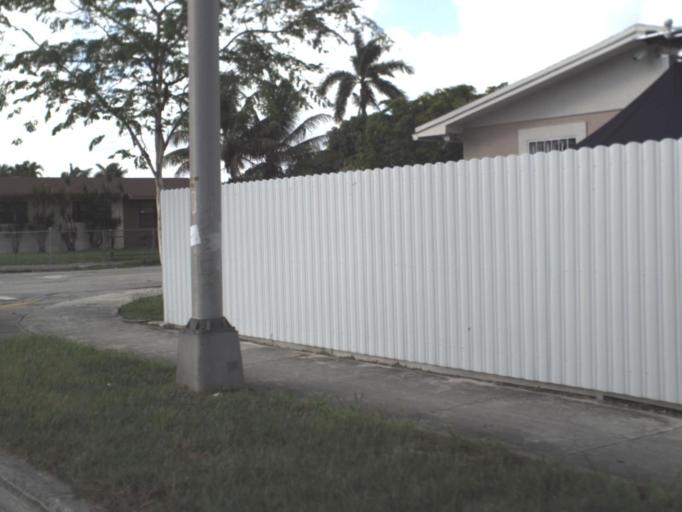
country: US
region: Florida
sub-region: Miami-Dade County
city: Leisure City
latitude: 25.4996
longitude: -80.4293
